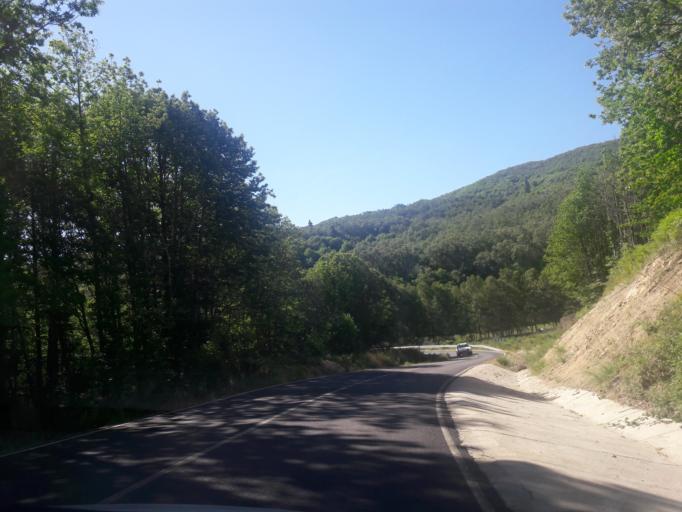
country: ES
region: Castille and Leon
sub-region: Provincia de Salamanca
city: Penacaballera
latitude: 40.3420
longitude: -5.8752
